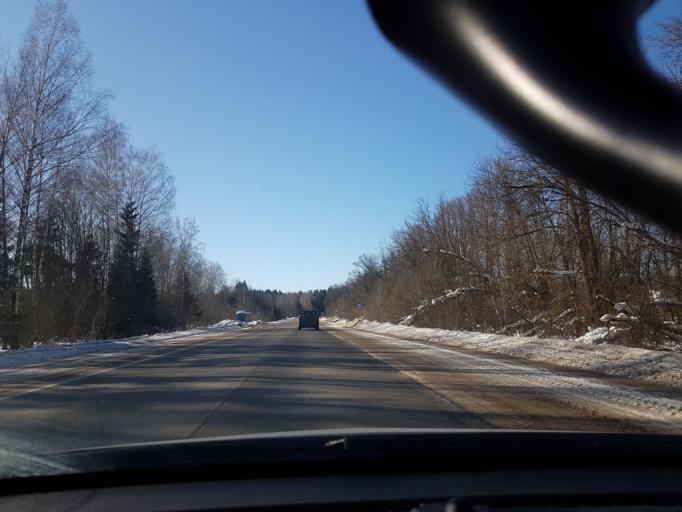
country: RU
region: Moskovskaya
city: Kostrovo
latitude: 55.9185
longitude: 36.6714
